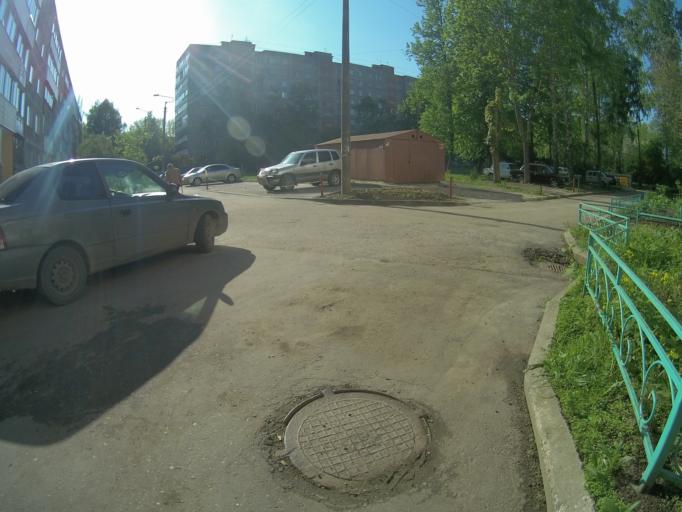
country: RU
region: Vladimir
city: Bogolyubovo
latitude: 56.1702
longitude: 40.4701
